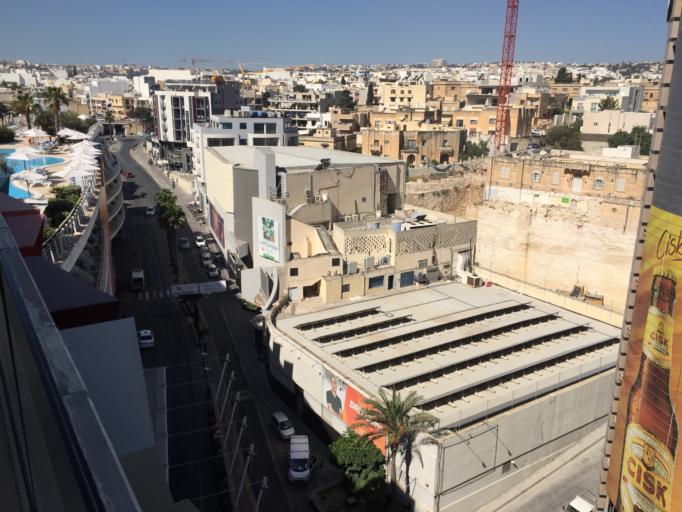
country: MT
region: Saint Julian
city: San Giljan
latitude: 35.9243
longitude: 14.4882
